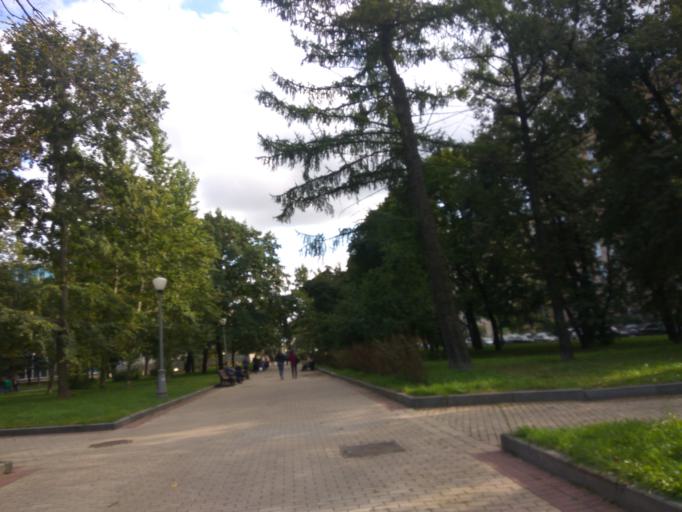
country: RU
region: Moscow
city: Vorob'yovo
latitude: 55.7396
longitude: 37.5215
